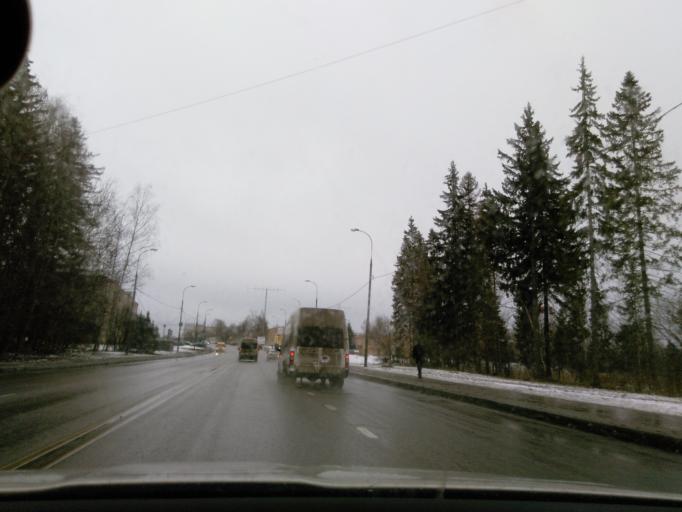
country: RU
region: Moskovskaya
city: Rzhavki
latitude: 55.9828
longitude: 37.2446
